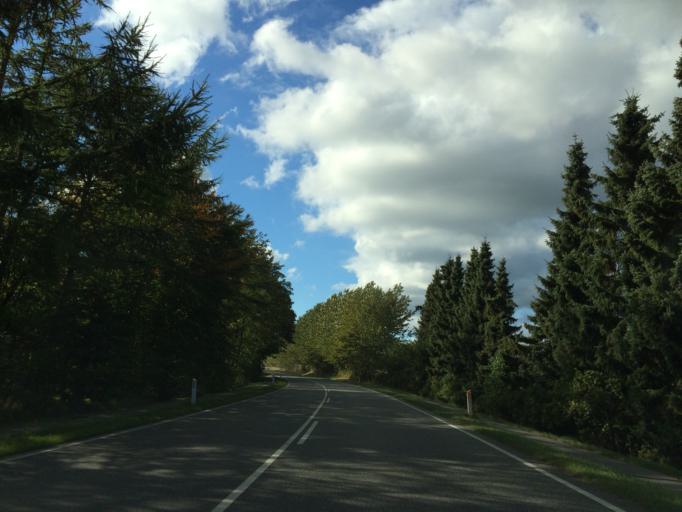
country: DK
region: Central Jutland
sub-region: Skanderborg Kommune
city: Ry
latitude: 56.0821
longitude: 9.7302
